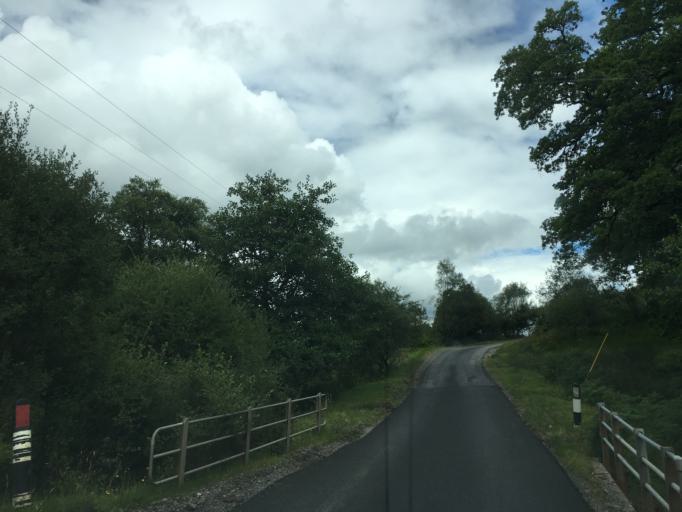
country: GB
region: Scotland
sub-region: Argyll and Bute
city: Oban
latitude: 56.3226
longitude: -5.2222
